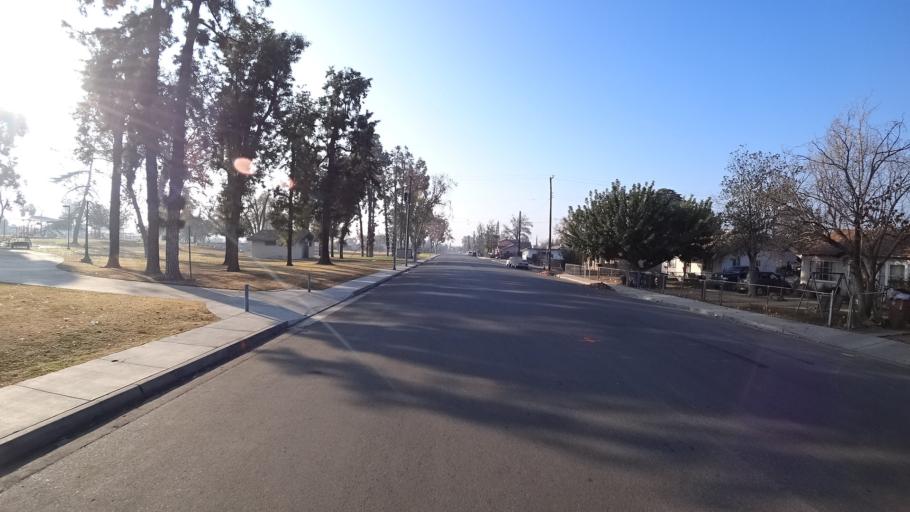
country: US
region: California
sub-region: Kern County
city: Bakersfield
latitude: 35.3899
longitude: -118.9866
